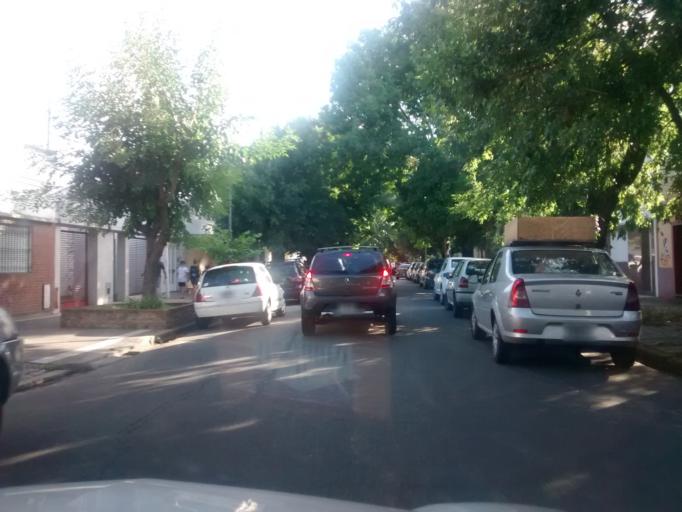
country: AR
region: Buenos Aires
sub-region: Partido de La Plata
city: La Plata
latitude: -34.9373
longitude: -57.9390
